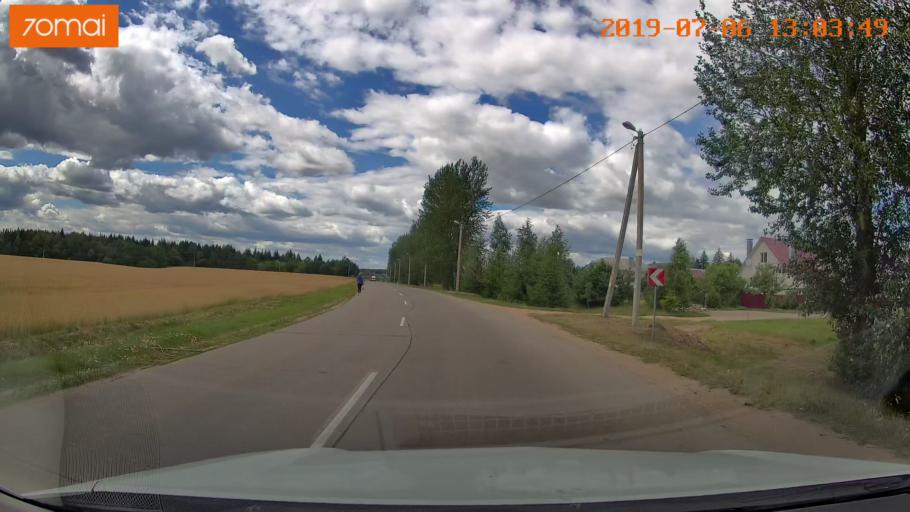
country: BY
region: Minsk
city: Dzyarzhynsk
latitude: 53.6901
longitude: 27.0954
